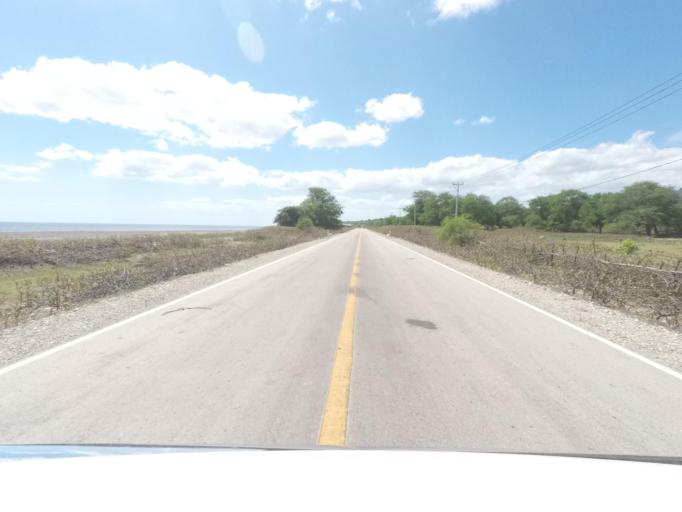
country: TL
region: Baucau
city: Baucau
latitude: -8.4531
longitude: 126.6317
